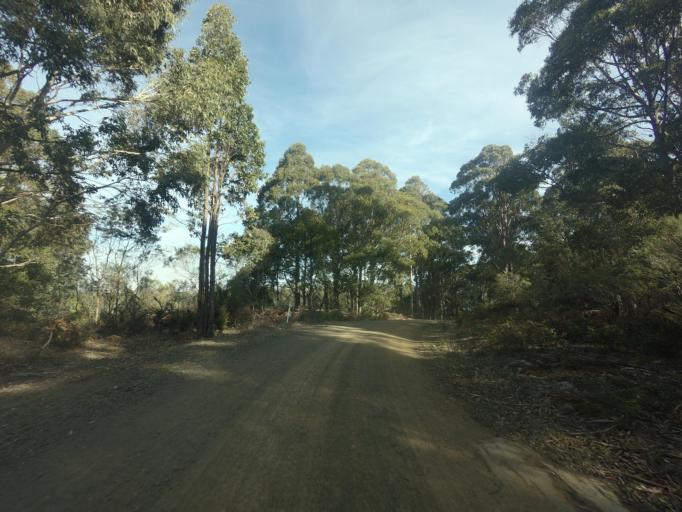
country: AU
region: Tasmania
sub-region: Sorell
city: Sorell
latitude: -42.5098
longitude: 147.4774
